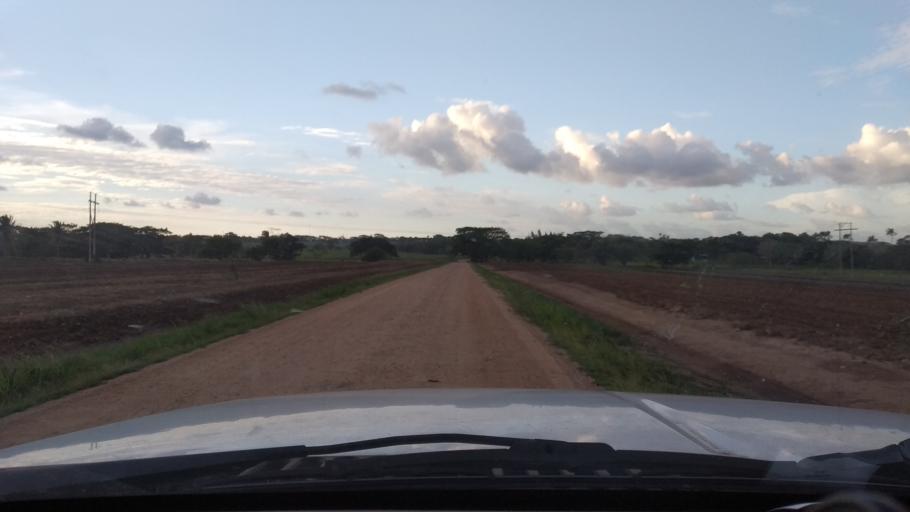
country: BZ
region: Cayo
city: San Ignacio
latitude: 17.2189
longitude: -88.9984
